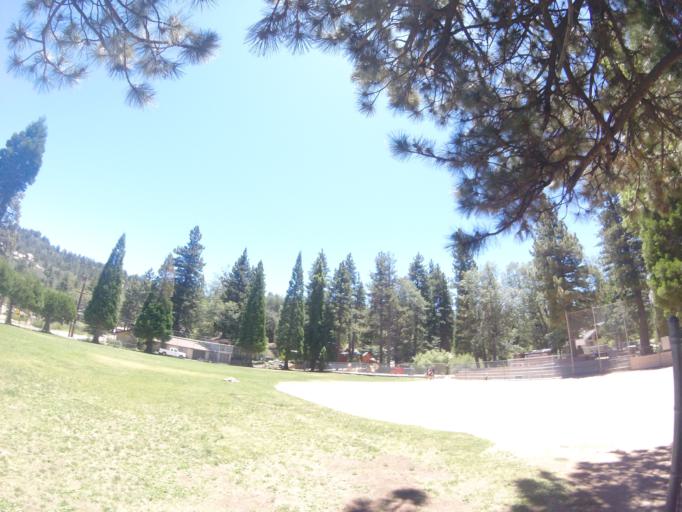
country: US
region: California
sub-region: San Bernardino County
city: Running Springs
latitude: 34.2118
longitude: -117.0784
